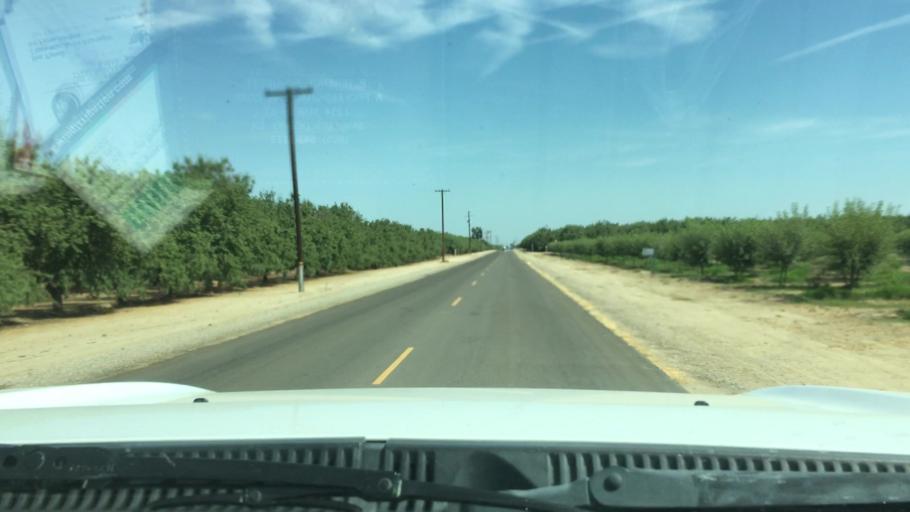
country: US
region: California
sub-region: Kern County
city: Wasco
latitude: 35.5235
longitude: -119.3499
